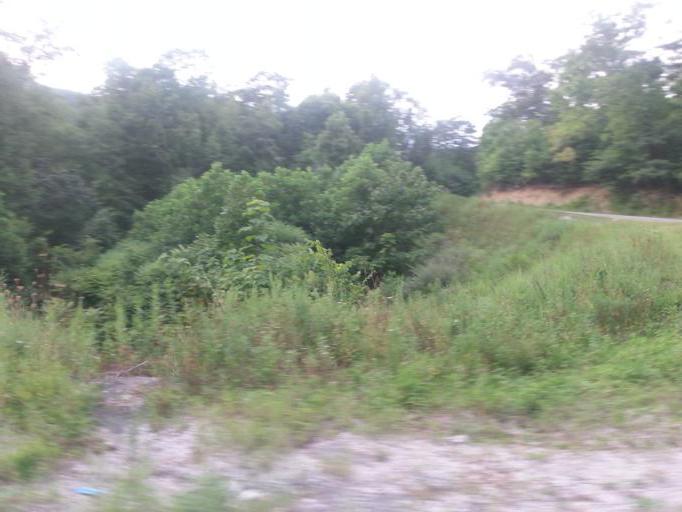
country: US
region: Tennessee
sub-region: Anderson County
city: Clinton
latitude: 36.1377
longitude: -84.2373
